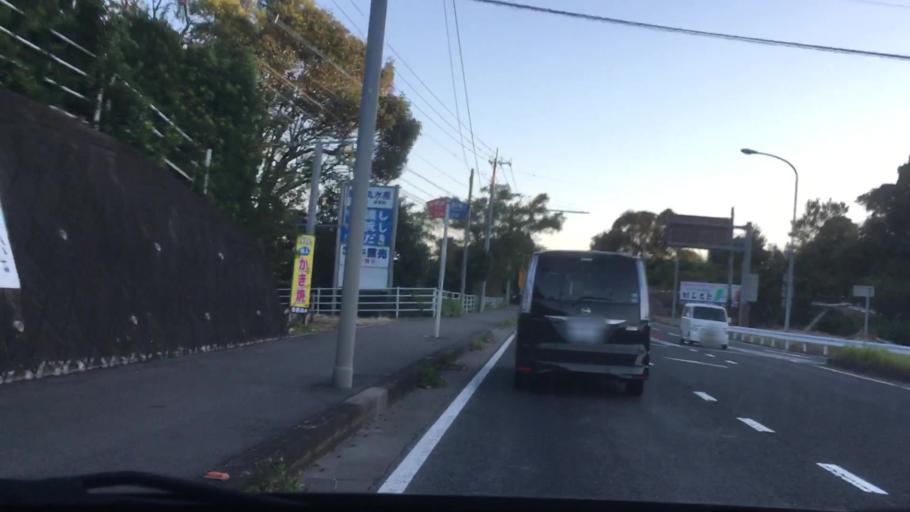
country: JP
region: Nagasaki
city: Sasebo
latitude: 33.0643
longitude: 129.7643
